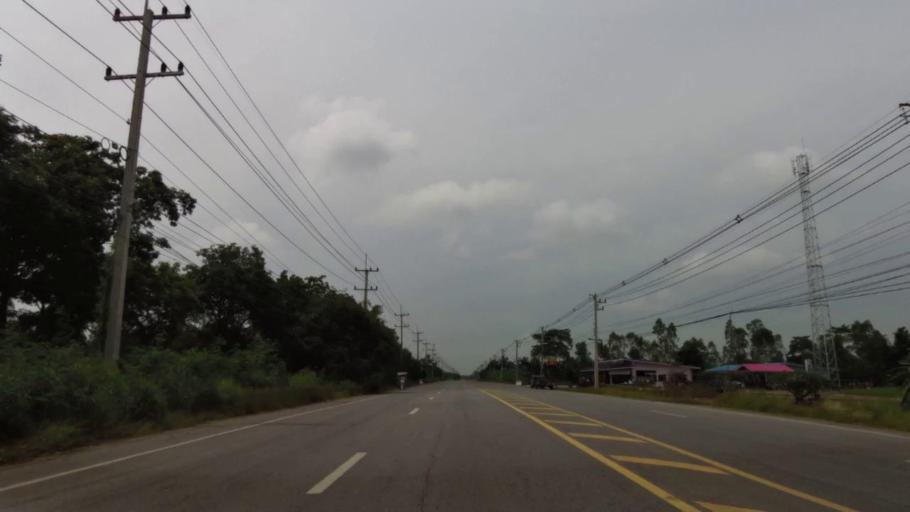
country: TH
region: Lop Buri
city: Ban Mi
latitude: 15.0621
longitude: 100.6079
